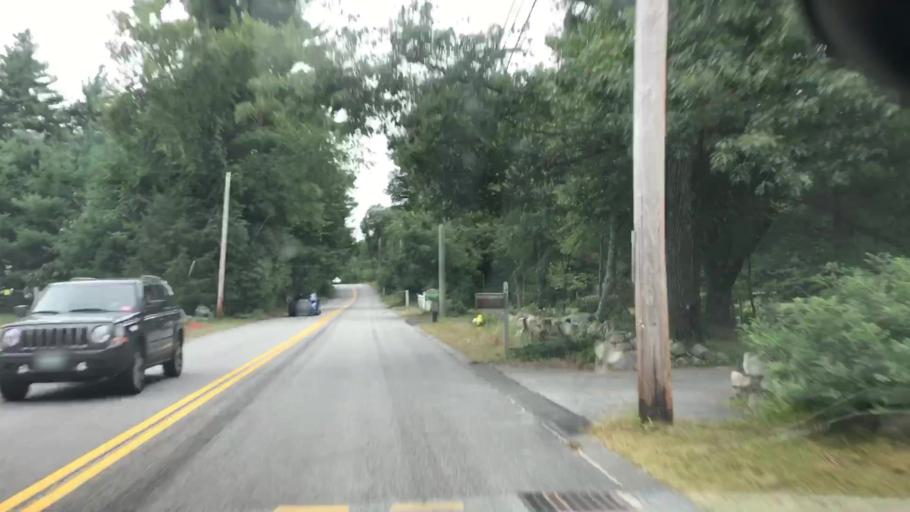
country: US
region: New Hampshire
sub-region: Hillsborough County
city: Hollis
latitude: 42.8113
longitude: -71.5580
